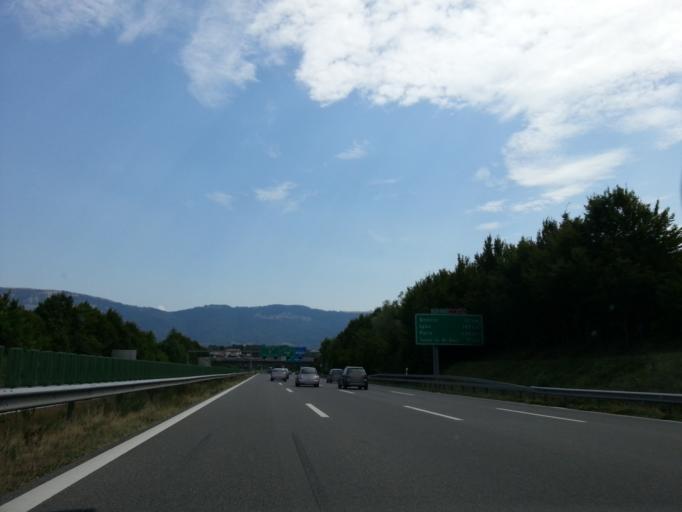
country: CH
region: Geneva
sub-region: Geneva
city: Confignon
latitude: 46.1686
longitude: 6.0952
